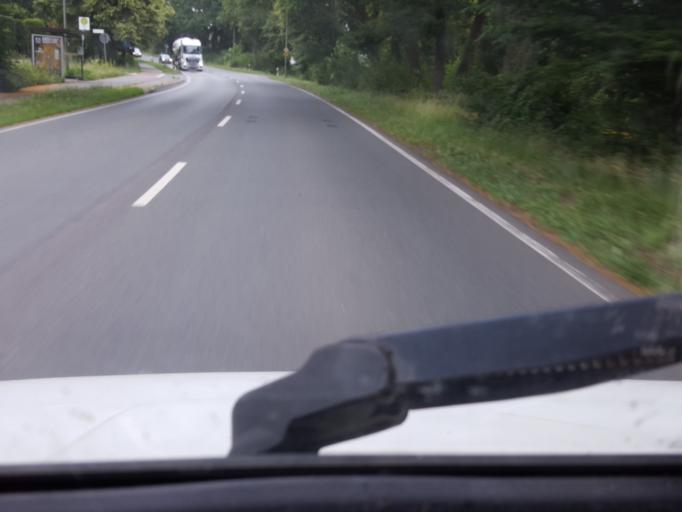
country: DE
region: North Rhine-Westphalia
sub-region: Regierungsbezirk Detmold
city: Minden
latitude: 52.3156
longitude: 8.9164
